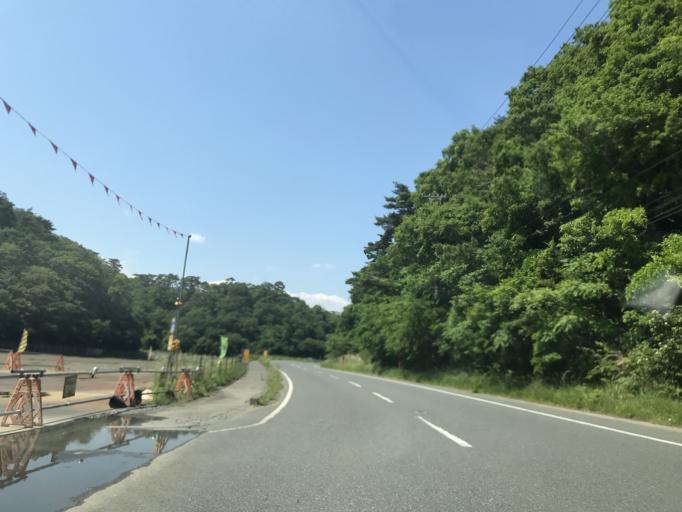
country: JP
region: Miyagi
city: Matsushima
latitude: 38.3462
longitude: 141.1542
